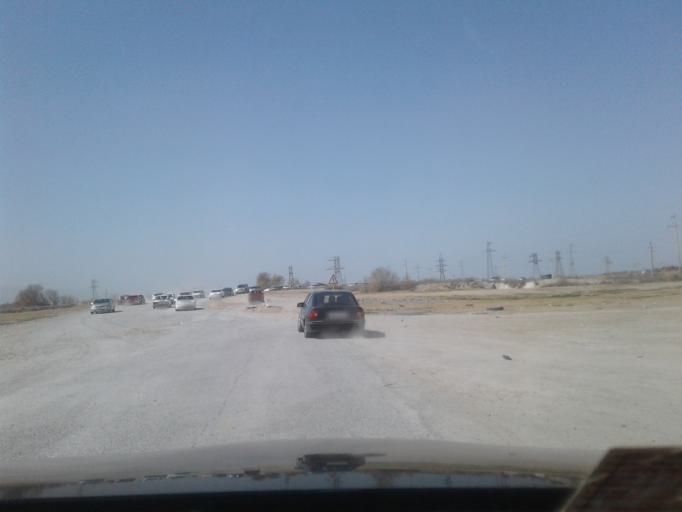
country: TM
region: Ahal
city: Abadan
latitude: 38.1772
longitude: 57.9808
